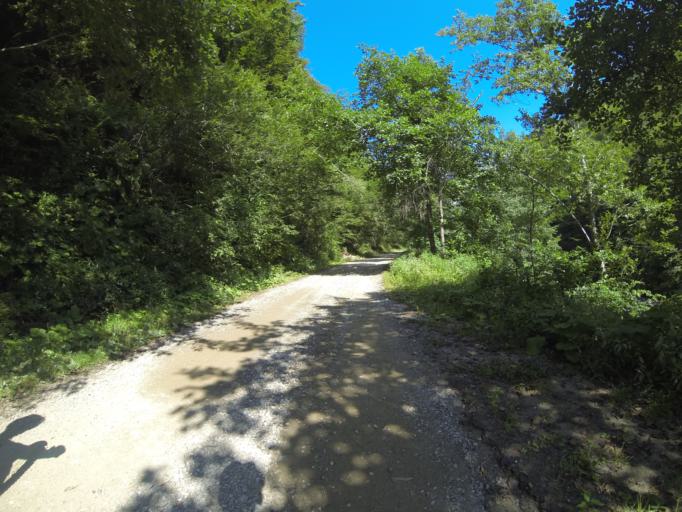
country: RO
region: Valcea
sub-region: Comuna Costesti
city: Bistrita
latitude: 45.2427
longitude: 23.9979
